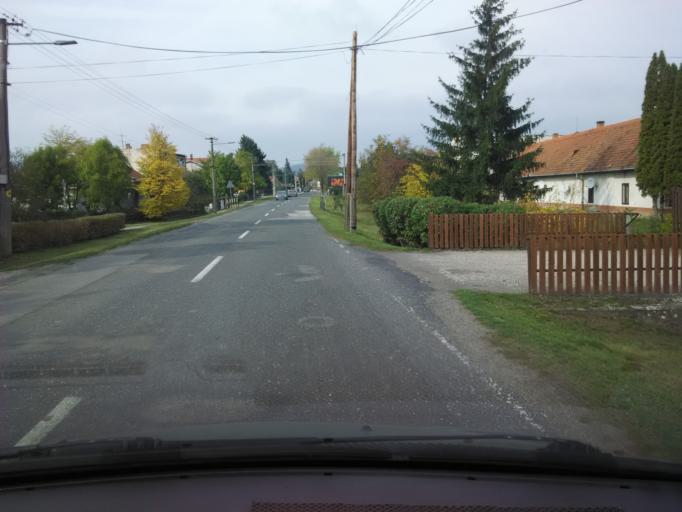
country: SK
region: Nitriansky
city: Tlmace
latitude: 48.2478
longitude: 18.5171
